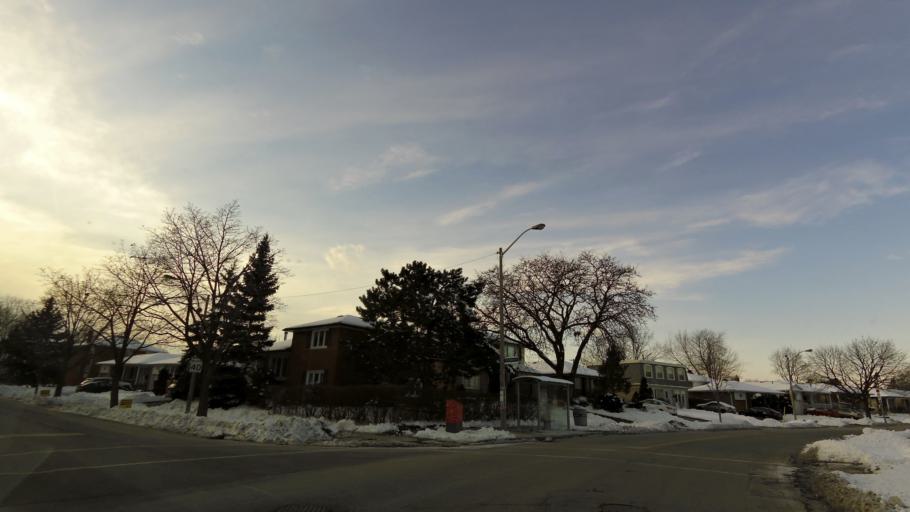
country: CA
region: Ontario
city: Etobicoke
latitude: 43.6551
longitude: -79.5763
